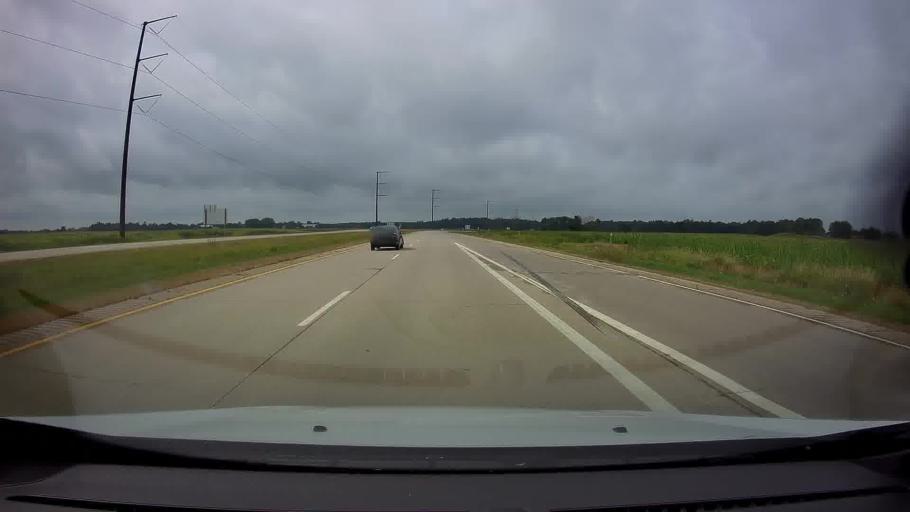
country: US
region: Wisconsin
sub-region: Shawano County
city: Shawano
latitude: 44.7561
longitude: -88.5726
